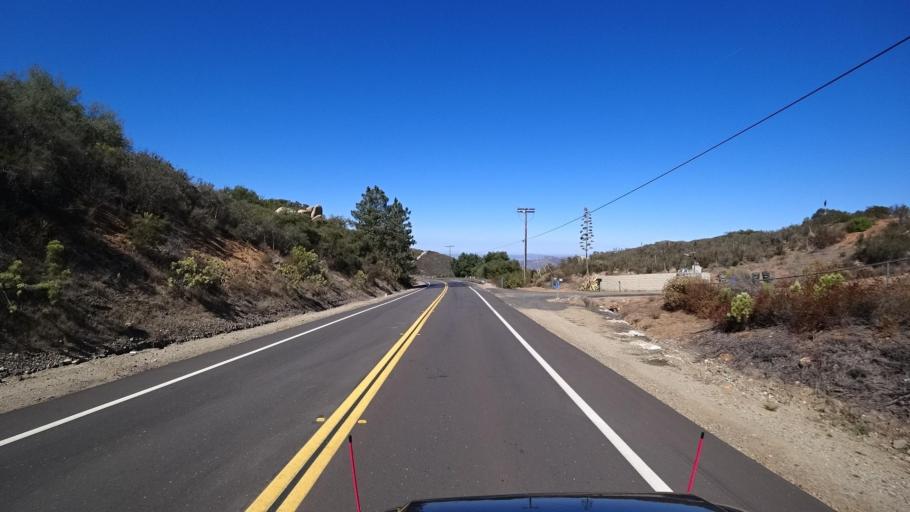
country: US
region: California
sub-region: San Diego County
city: Jamul
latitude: 32.7334
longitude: -116.7986
